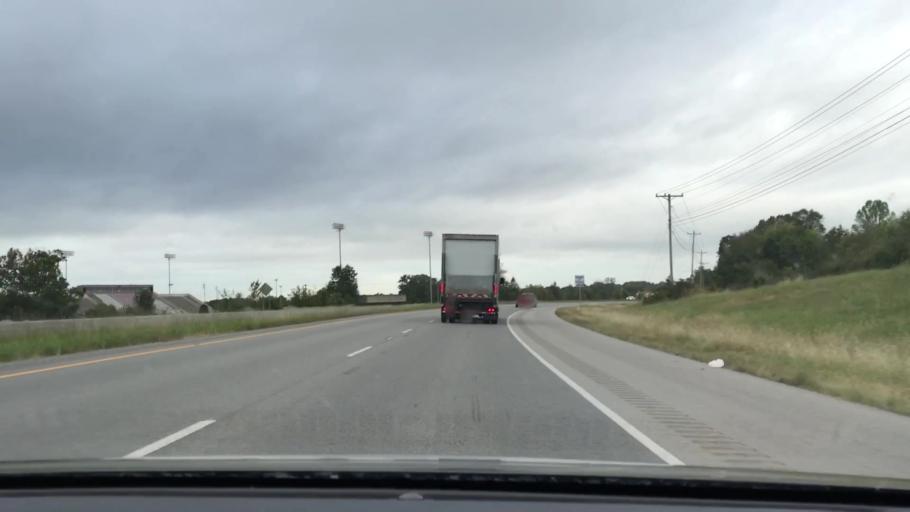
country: US
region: Kentucky
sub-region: Christian County
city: Hopkinsville
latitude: 36.8181
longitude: -87.4980
